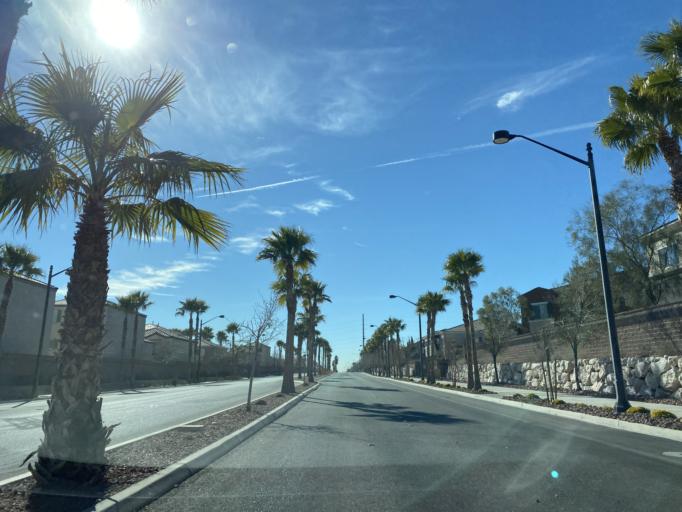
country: US
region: Nevada
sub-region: Clark County
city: Summerlin South
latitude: 36.3022
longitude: -115.2969
